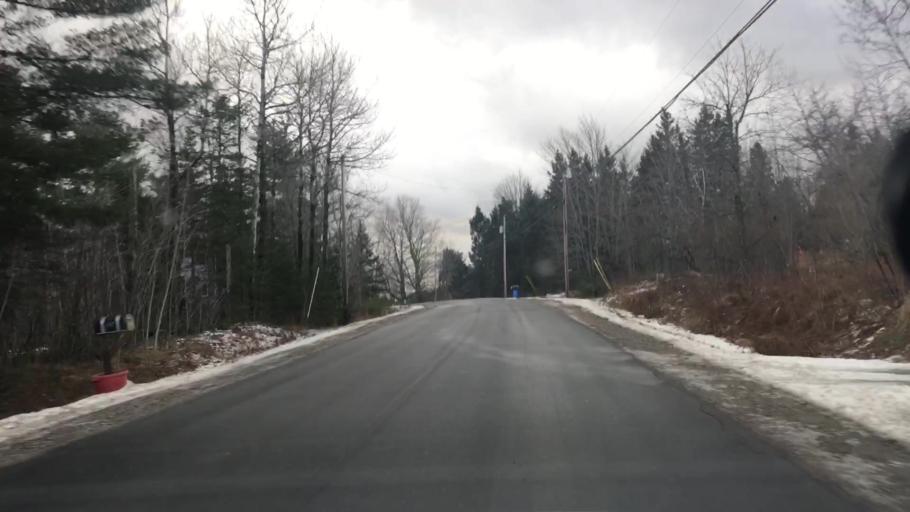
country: US
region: Maine
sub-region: Hancock County
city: Dedham
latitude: 44.6606
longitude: -68.7046
